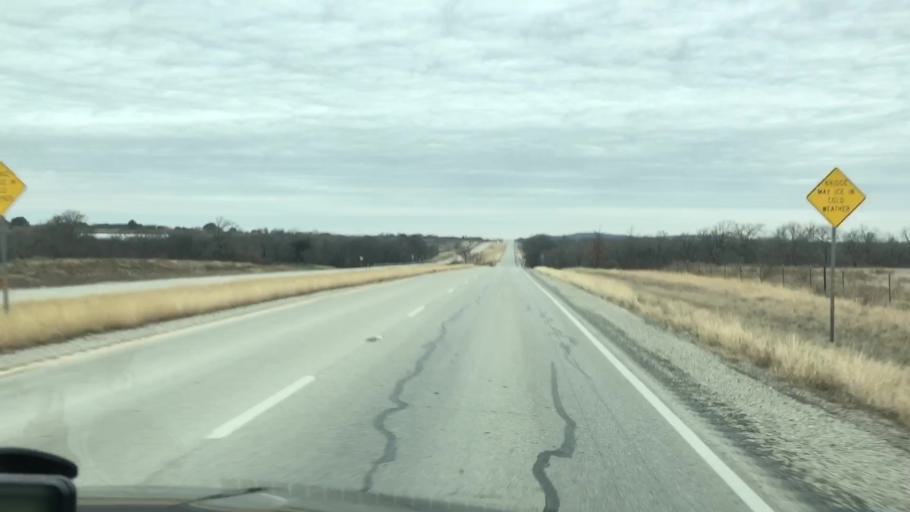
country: US
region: Texas
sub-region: Jack County
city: Jacksboro
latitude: 33.2392
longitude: -98.2145
